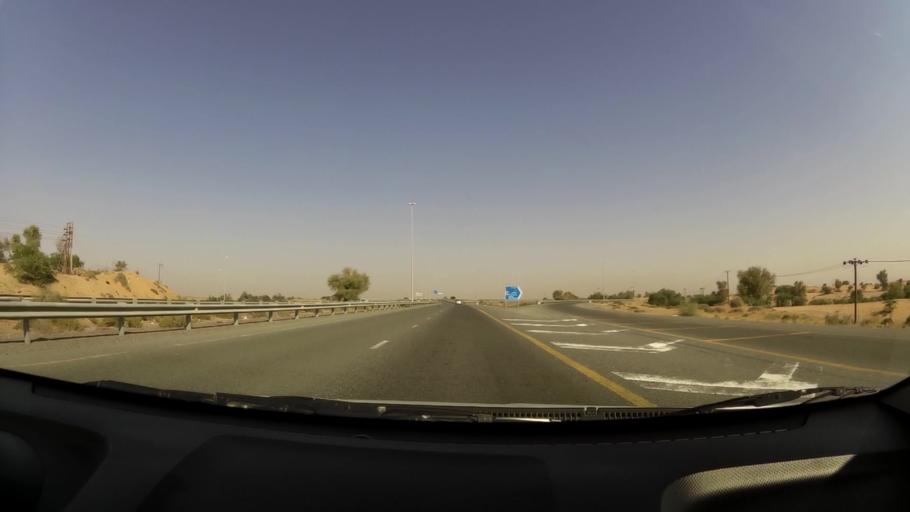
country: AE
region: Umm al Qaywayn
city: Umm al Qaywayn
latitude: 25.4555
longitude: 55.6099
